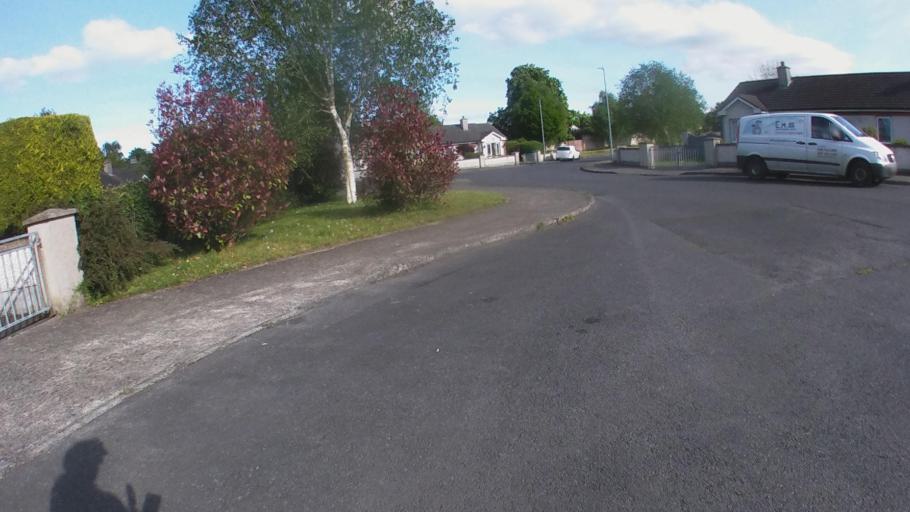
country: IE
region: Leinster
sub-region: County Carlow
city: Carlow
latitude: 52.8427
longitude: -6.9316
